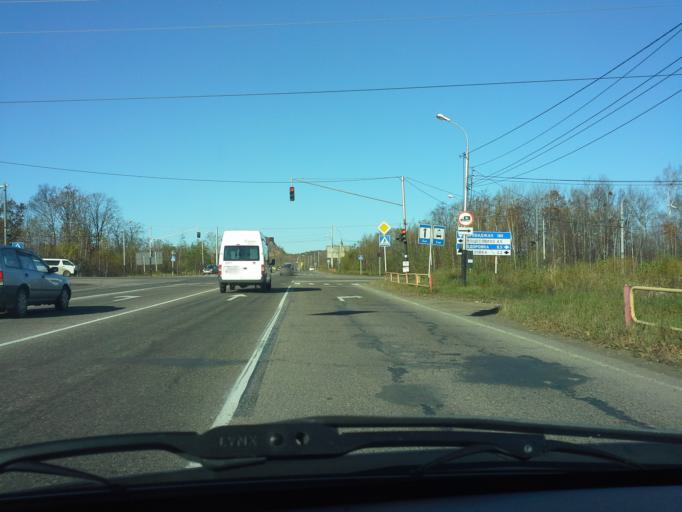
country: RU
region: Khabarovsk Krai
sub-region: Khabarovskiy Rayon
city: Khabarovsk
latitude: 48.5471
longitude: 135.0966
